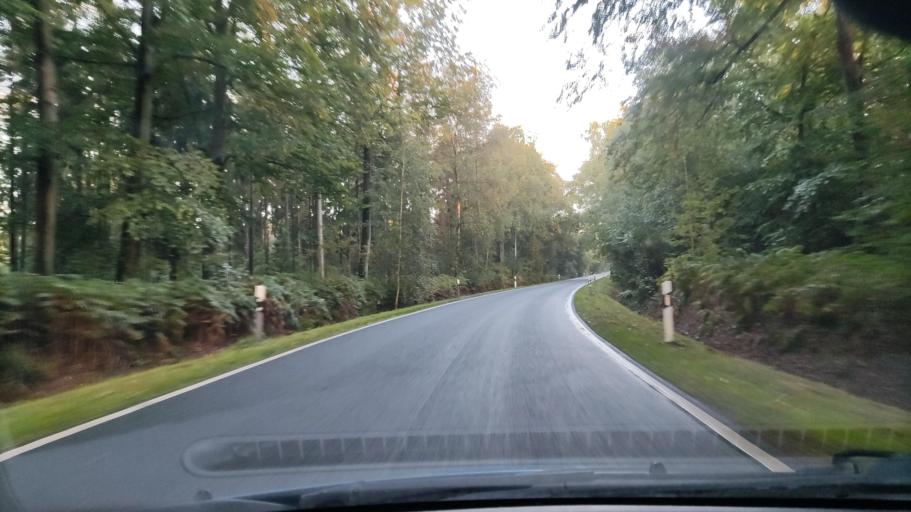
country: DE
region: Mecklenburg-Vorpommern
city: Lubtheen
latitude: 53.3023
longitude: 10.9866
